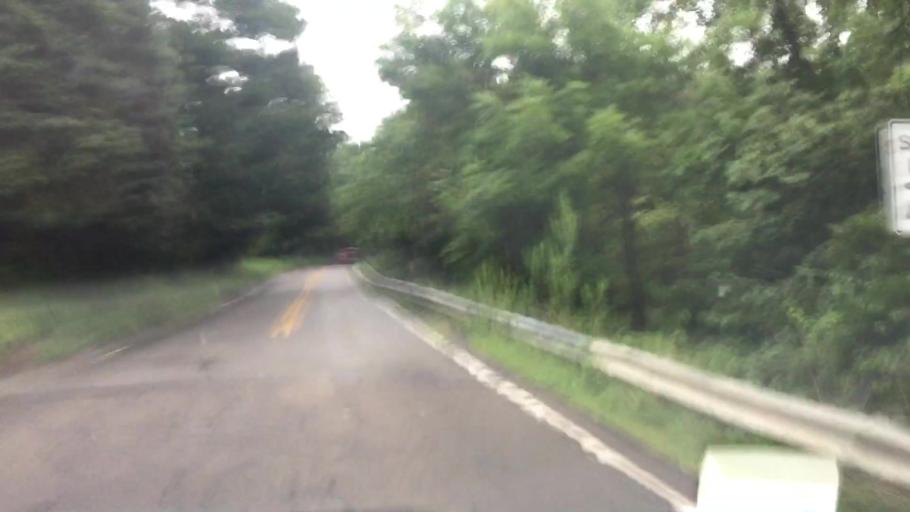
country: US
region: Pennsylvania
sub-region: Allegheny County
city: Bridgeville
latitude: 40.3580
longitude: -80.0978
